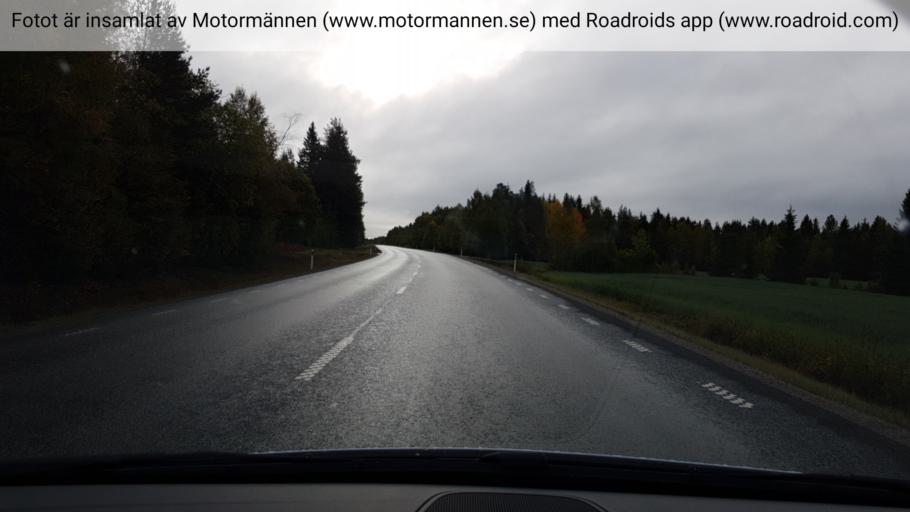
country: SE
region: Vaesterbotten
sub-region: Umea Kommun
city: Roback
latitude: 63.8544
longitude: 20.0998
